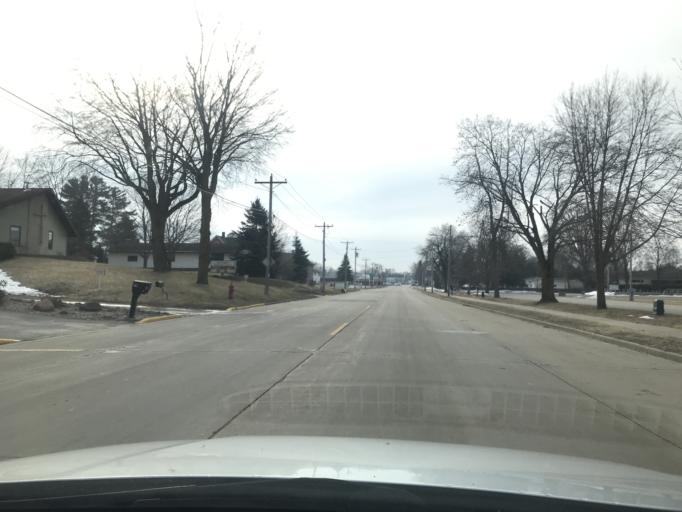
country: US
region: Wisconsin
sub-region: Oconto County
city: Oconto Falls
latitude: 44.8805
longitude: -88.1498
